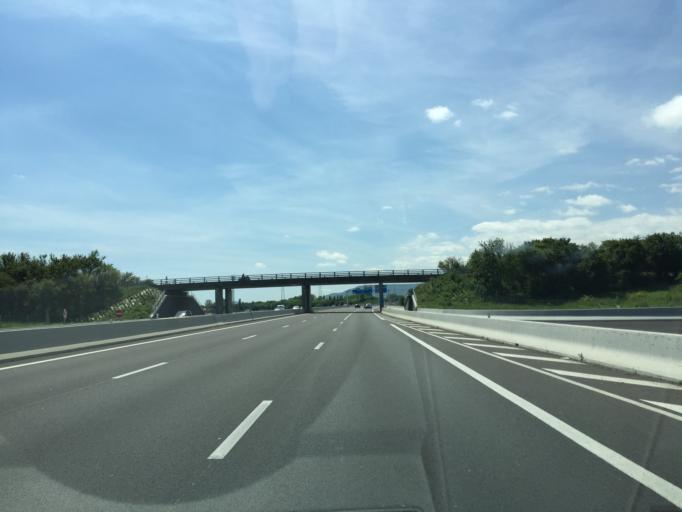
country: FR
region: Auvergne
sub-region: Departement du Puy-de-Dome
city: Gerzat
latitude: 45.8158
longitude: 3.1555
